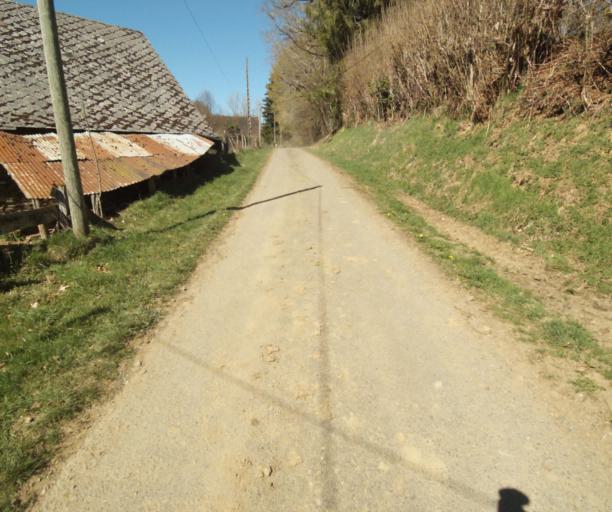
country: FR
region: Limousin
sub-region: Departement de la Correze
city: Saint-Clement
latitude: 45.3929
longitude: 1.6605
